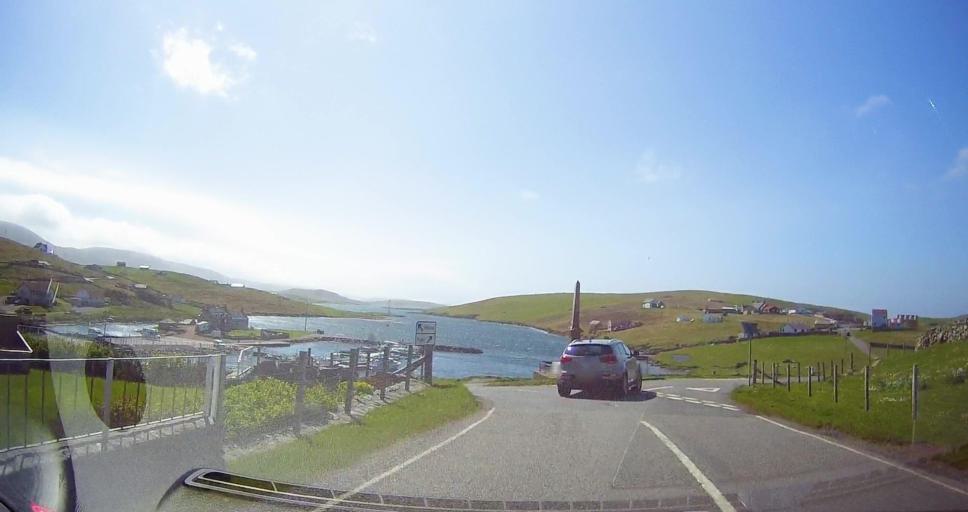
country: GB
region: Scotland
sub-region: Shetland Islands
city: Sandwick
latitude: 60.0831
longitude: -1.3321
